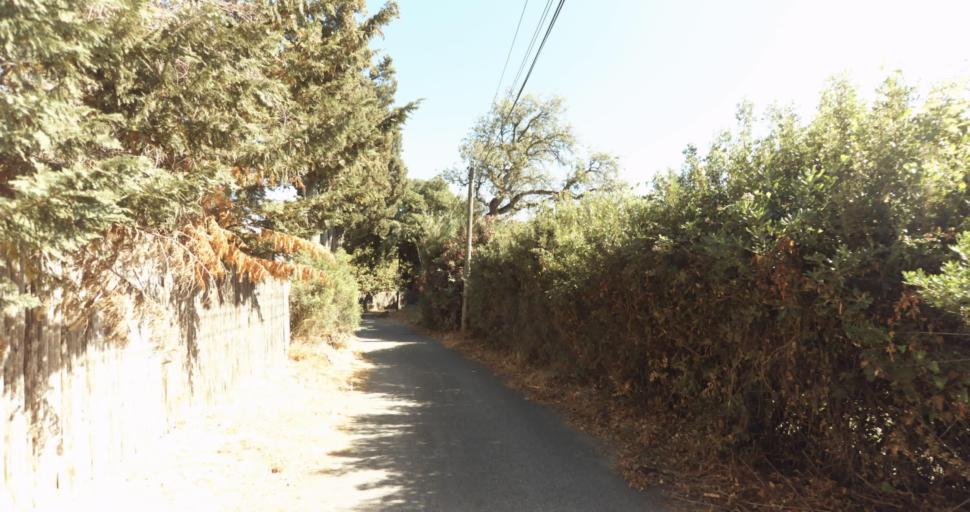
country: FR
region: Provence-Alpes-Cote d'Azur
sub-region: Departement du Var
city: Saint-Tropez
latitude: 43.2612
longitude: 6.6174
